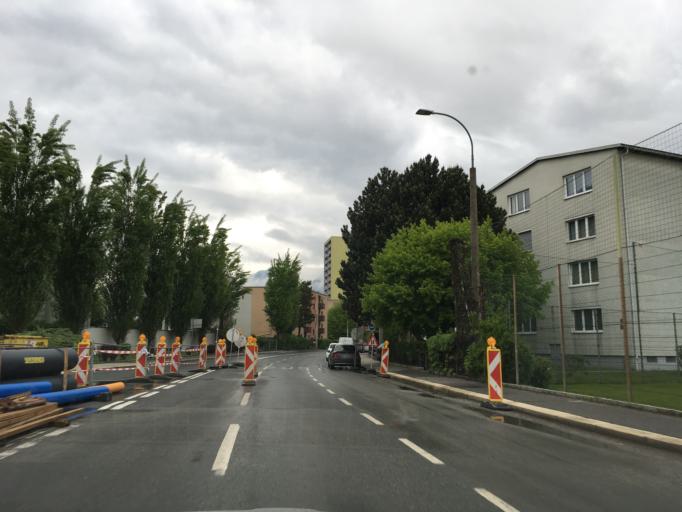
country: AT
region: Tyrol
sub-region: Politischer Bezirk Innsbruck Land
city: Ampass
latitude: 47.2743
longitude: 11.4355
